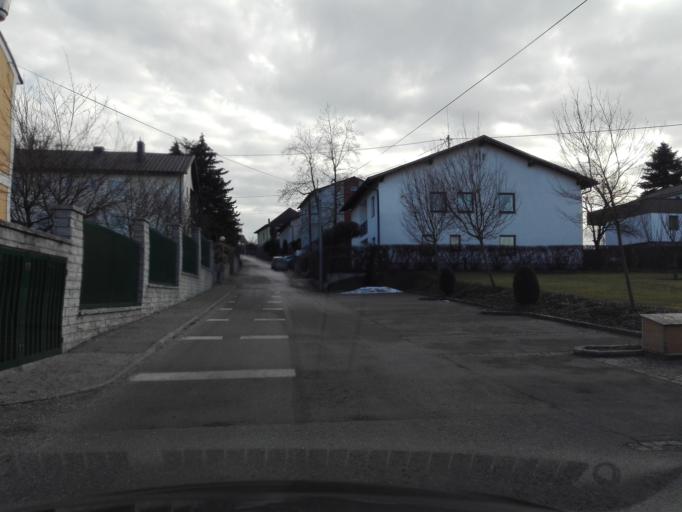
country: AT
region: Upper Austria
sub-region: Politischer Bezirk Perg
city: Perg
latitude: 48.2725
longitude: 14.5853
